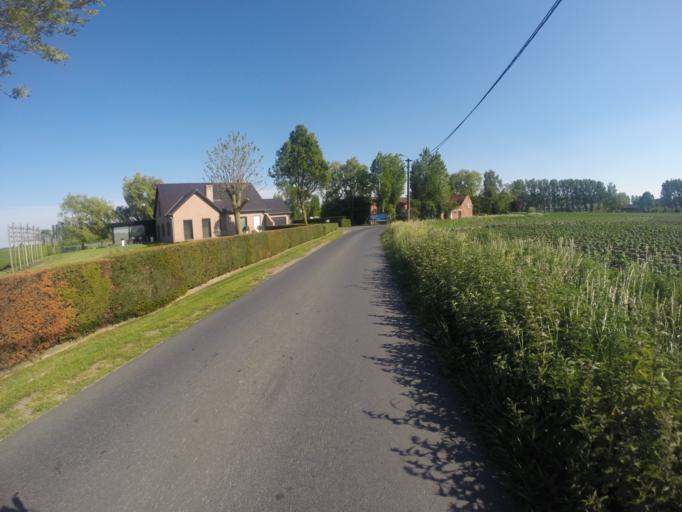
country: BE
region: Flanders
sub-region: Provincie Oost-Vlaanderen
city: Aalter
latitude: 51.0706
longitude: 3.4231
